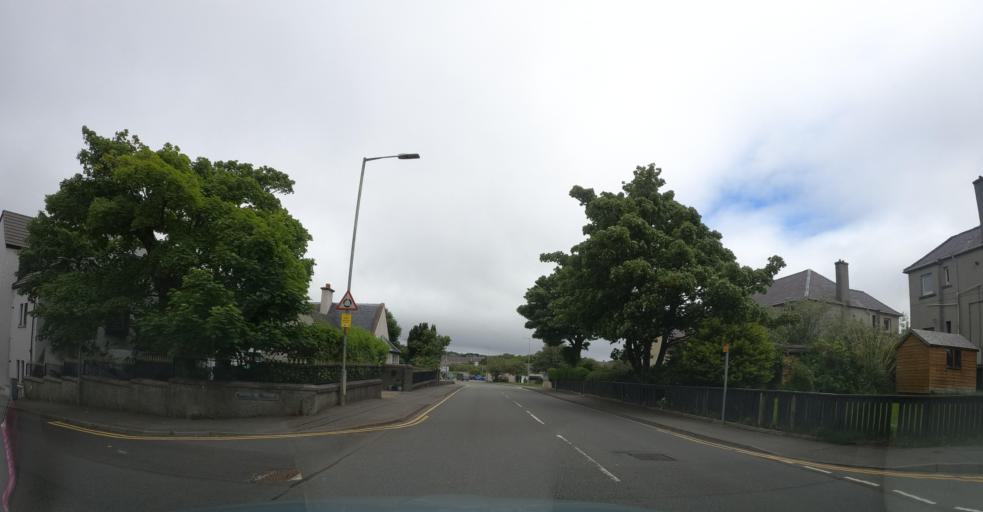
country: GB
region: Scotland
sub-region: Eilean Siar
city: Isle of Lewis
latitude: 58.2149
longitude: -6.3844
